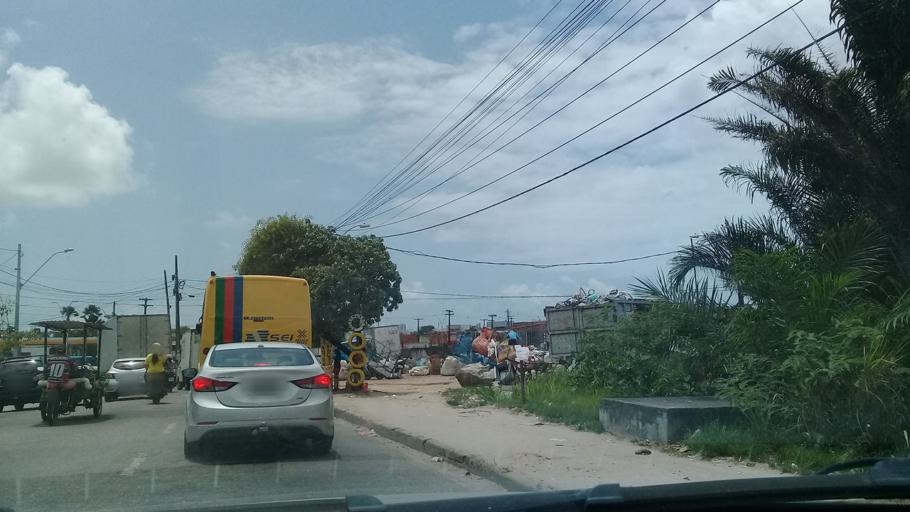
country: BR
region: Pernambuco
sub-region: Recife
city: Recife
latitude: -8.1077
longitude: -34.9281
